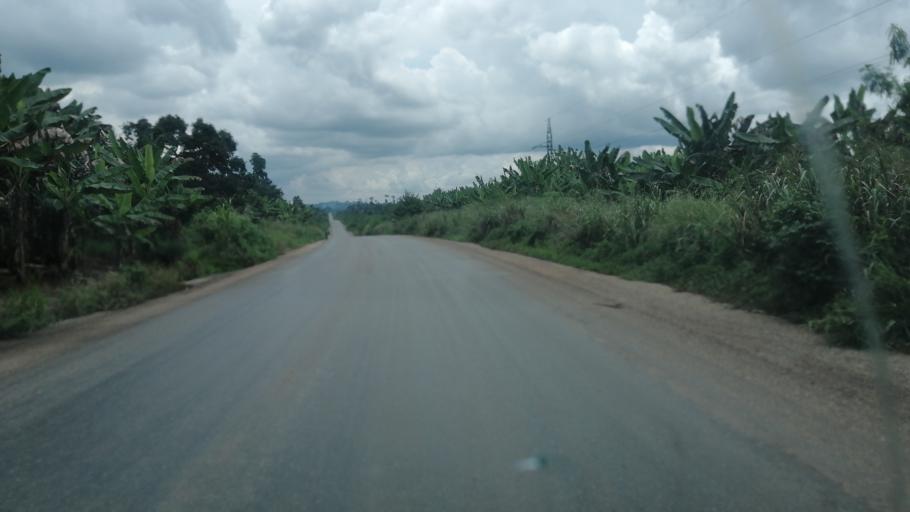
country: GH
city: Duayaw Nkwanta
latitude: 6.9108
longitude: -2.3926
